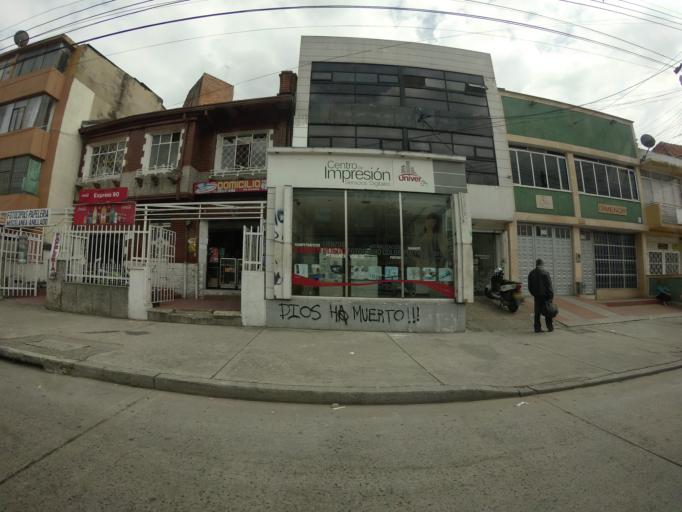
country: CO
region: Bogota D.C.
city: Bogota
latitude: 4.6206
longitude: -74.0732
